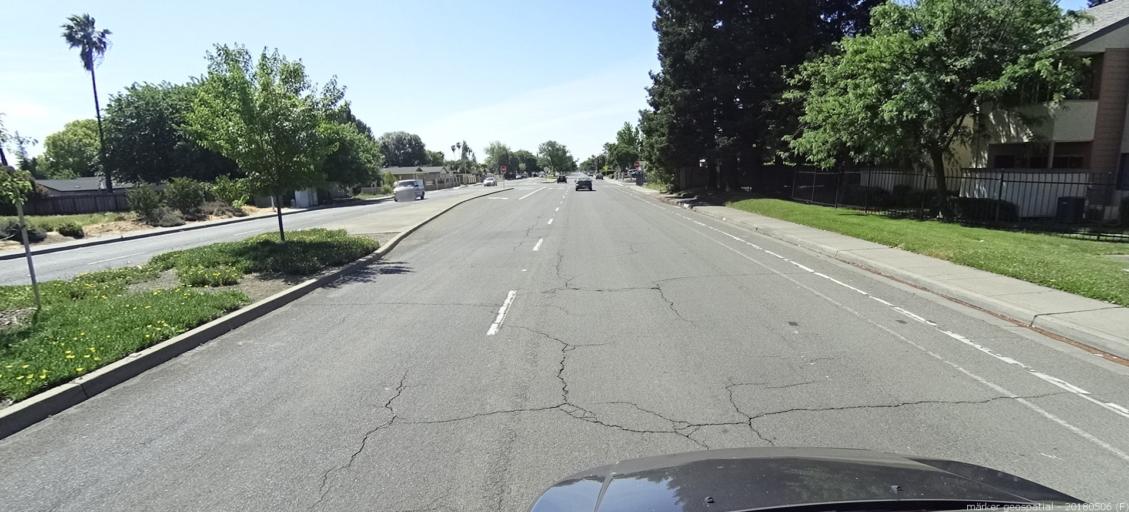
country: US
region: California
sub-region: Sacramento County
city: Parkway
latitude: 38.4722
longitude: -121.4359
